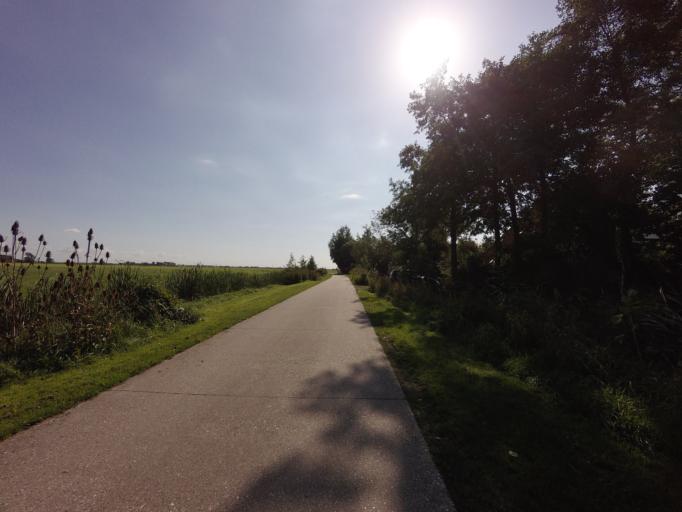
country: NL
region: Friesland
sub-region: Gemeente Littenseradiel
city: Makkum
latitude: 53.0985
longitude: 5.6485
